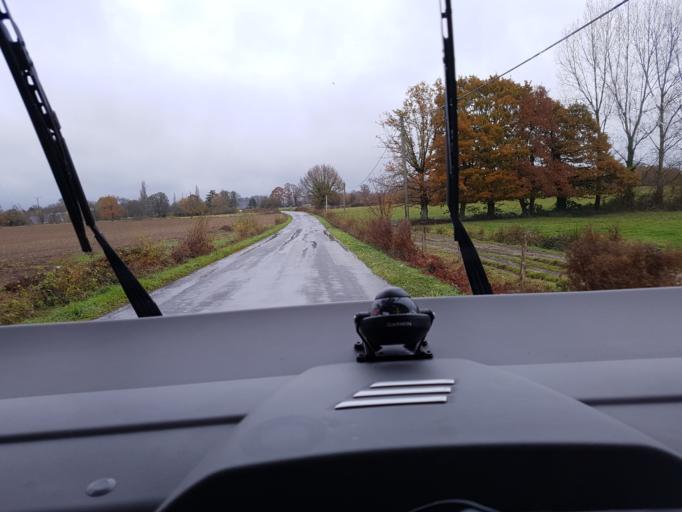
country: FR
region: Pays de la Loire
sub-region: Departement de la Mayenne
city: Montenay
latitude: 48.3017
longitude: -0.8760
